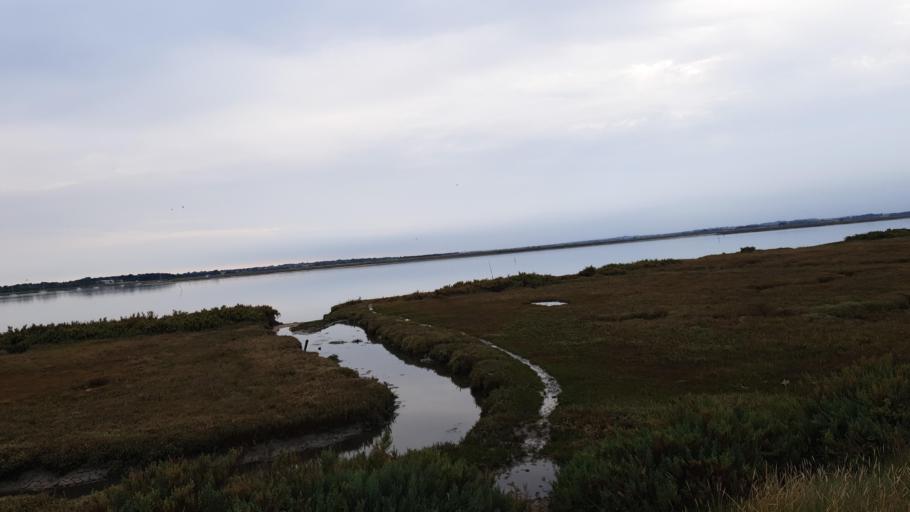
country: GB
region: England
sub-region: Essex
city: Brightlingsea
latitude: 51.8131
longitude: 1.0005
